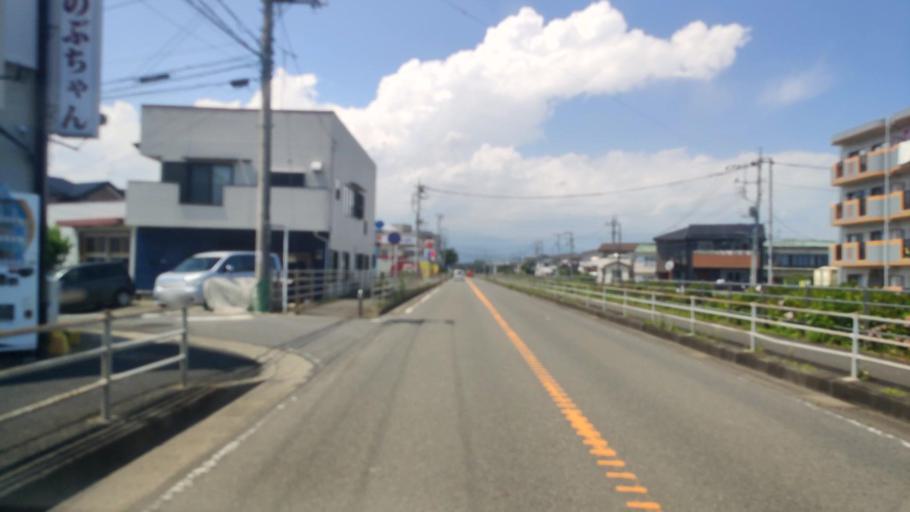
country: JP
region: Kanagawa
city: Hiratsuka
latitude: 35.3392
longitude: 139.3093
